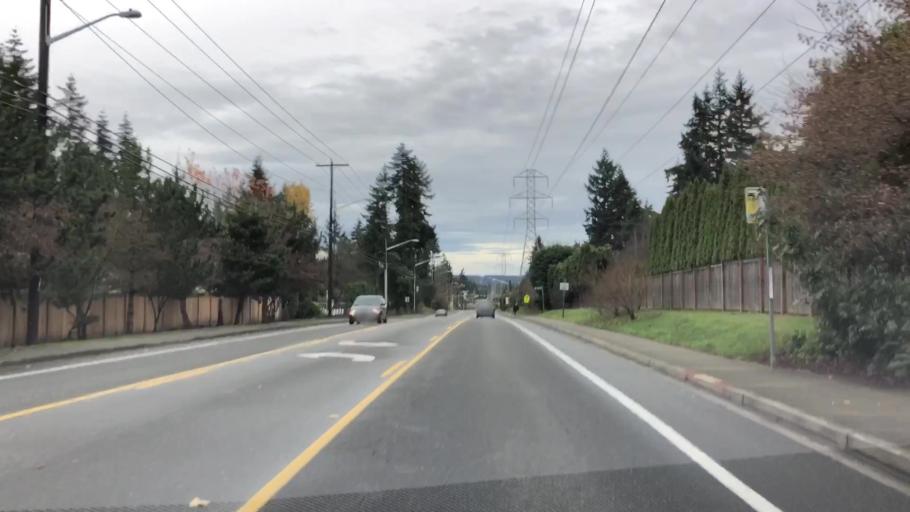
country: US
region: Washington
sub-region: King County
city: Kingsgate
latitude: 47.7288
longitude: -122.1756
